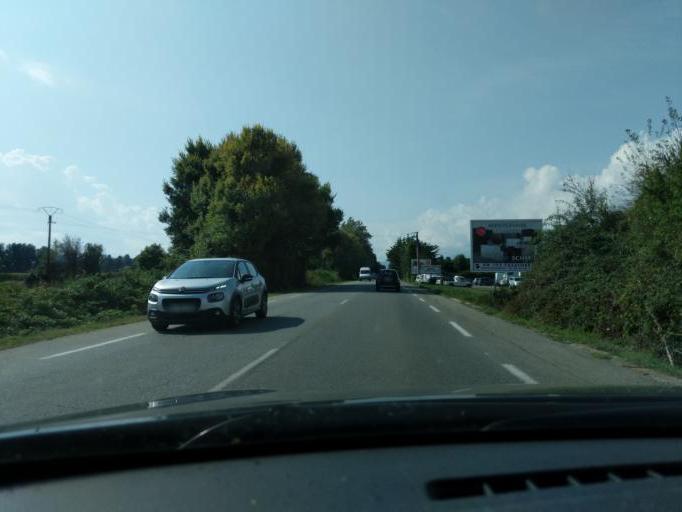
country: FR
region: Corsica
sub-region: Departement de la Haute-Corse
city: Ghisonaccia
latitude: 41.9743
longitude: 9.3991
